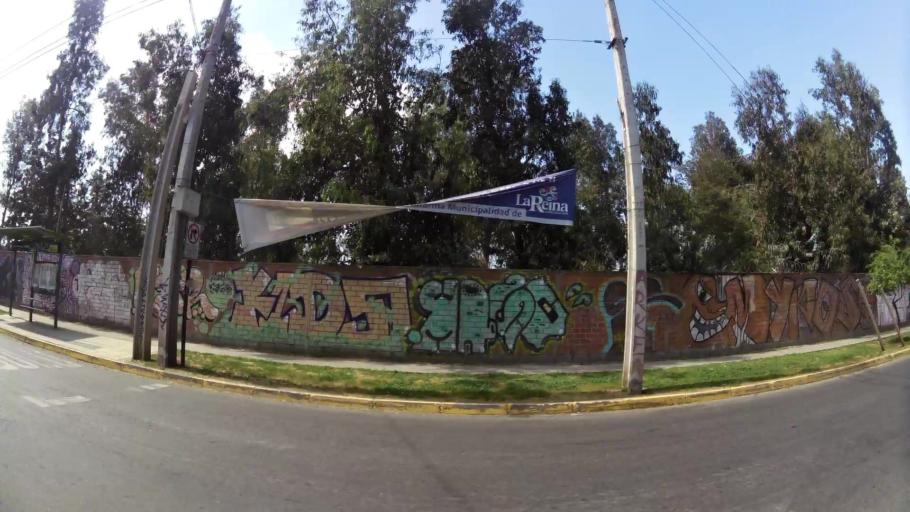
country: CL
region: Santiago Metropolitan
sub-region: Provincia de Santiago
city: Villa Presidente Frei, Nunoa, Santiago, Chile
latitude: -33.4588
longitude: -70.5410
